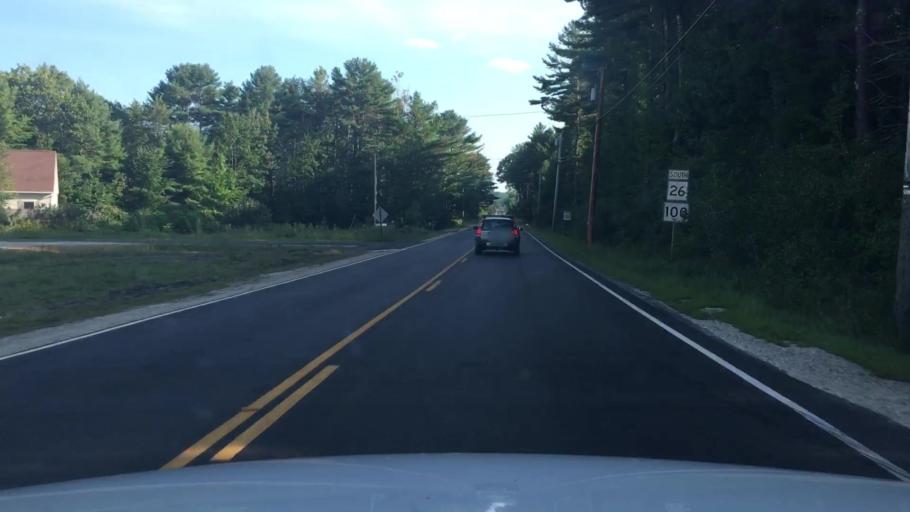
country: US
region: Maine
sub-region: Cumberland County
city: Cumberland Center
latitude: 43.7969
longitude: -70.3064
